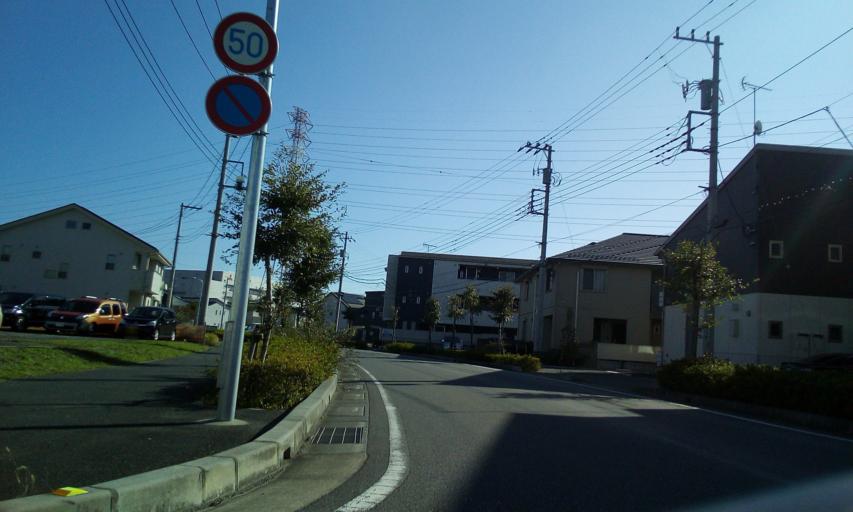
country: JP
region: Saitama
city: Yoshikawa
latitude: 35.8650
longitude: 139.8573
